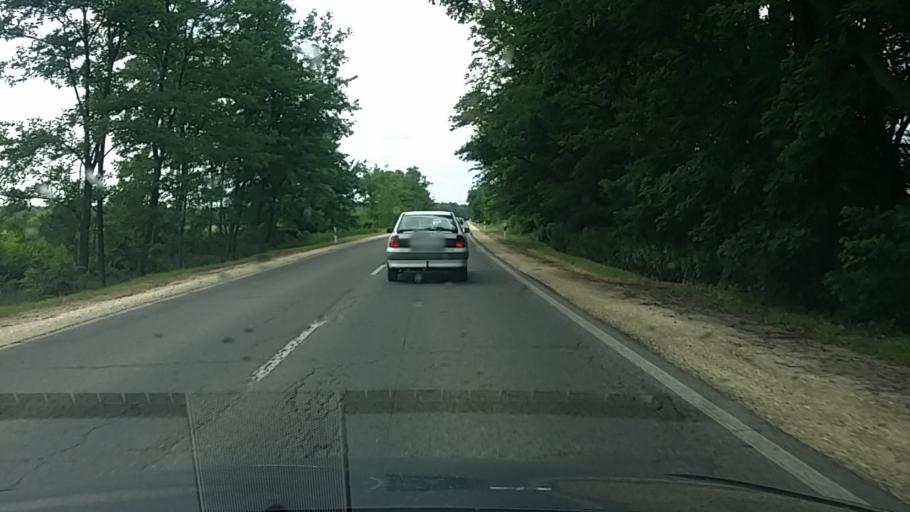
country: HU
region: Pest
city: Orkeny
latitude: 47.1414
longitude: 19.4017
